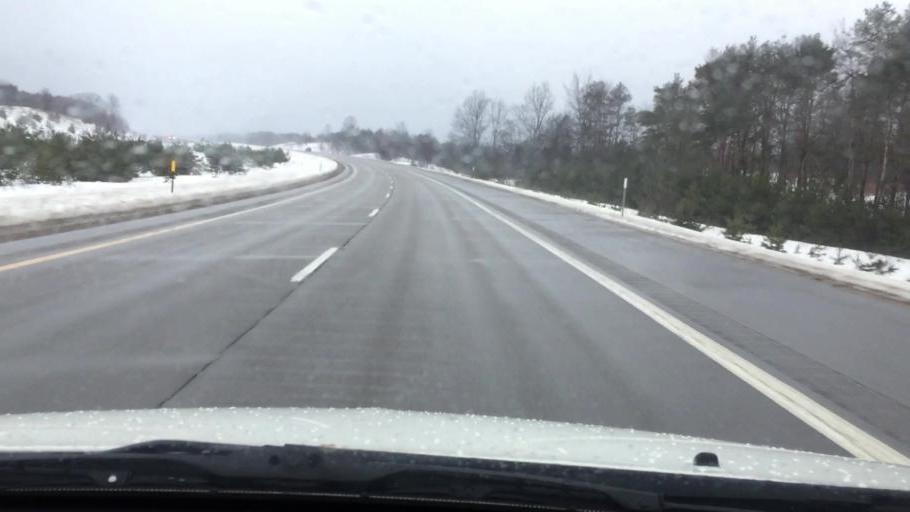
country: US
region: Michigan
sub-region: Wexford County
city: Manton
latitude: 44.3692
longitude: -85.4013
